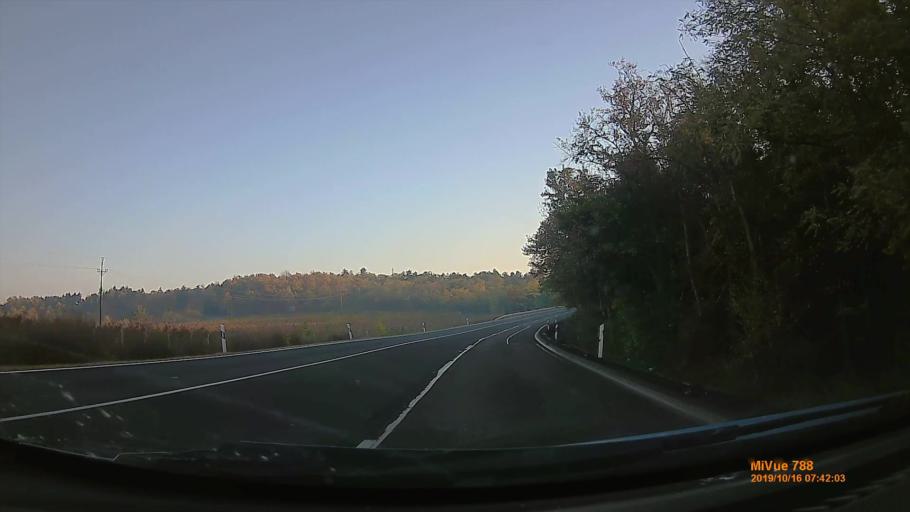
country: HU
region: Heves
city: Kerecsend
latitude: 47.8352
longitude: 20.3582
